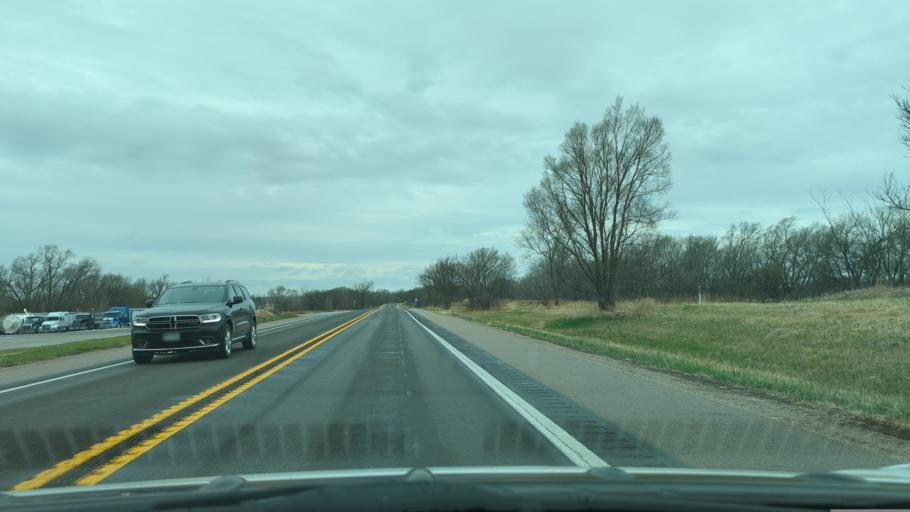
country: US
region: Nebraska
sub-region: Lancaster County
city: Waverly
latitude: 40.9563
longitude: -96.4477
